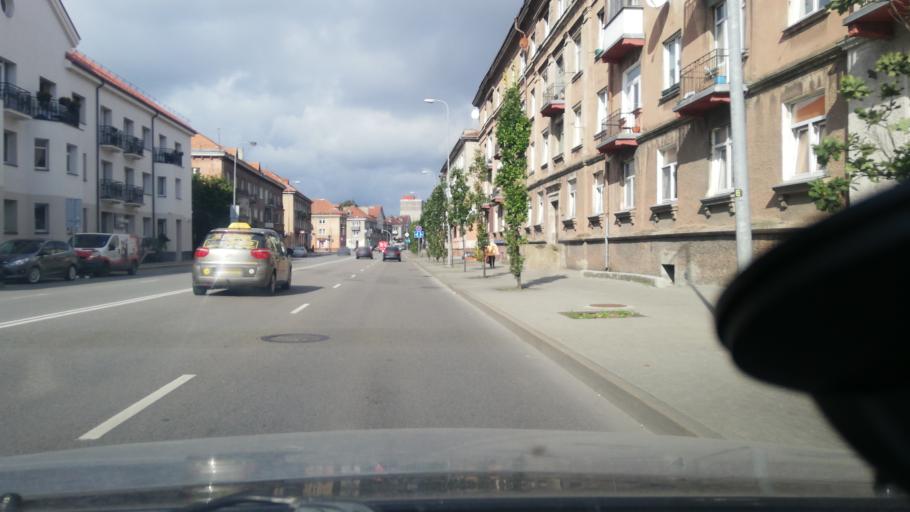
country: LT
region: Klaipedos apskritis
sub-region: Klaipeda
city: Klaipeda
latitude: 55.6765
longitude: 21.1540
